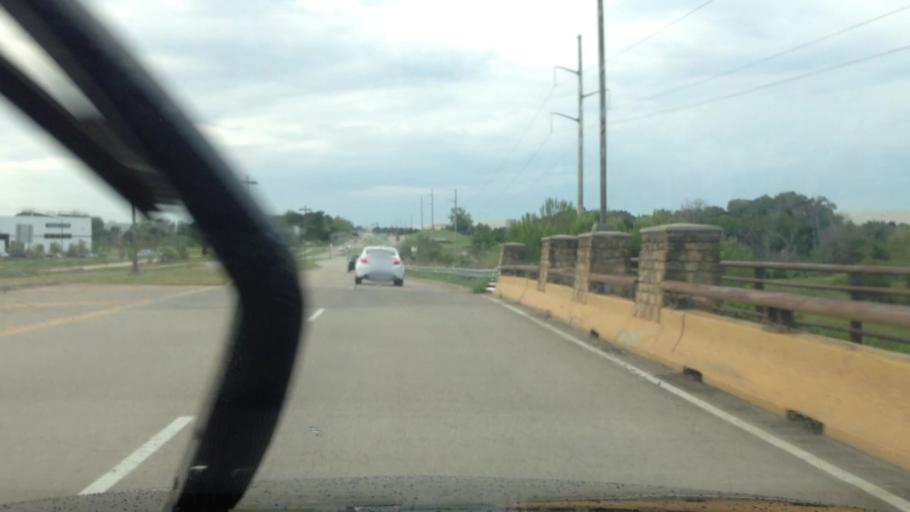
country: US
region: Texas
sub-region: Dallas County
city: Coppell
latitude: 32.9856
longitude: -97.0277
